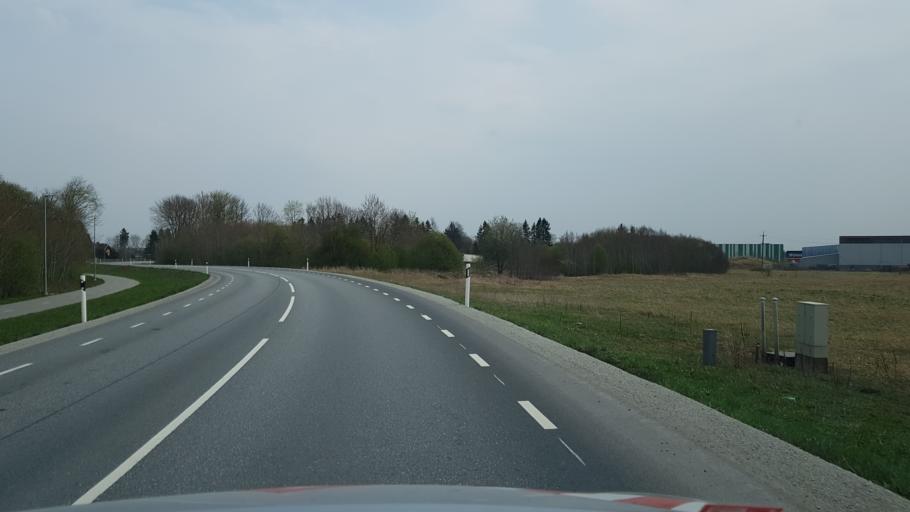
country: EE
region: Harju
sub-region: Rae vald
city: Jueri
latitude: 59.3698
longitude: 24.8618
